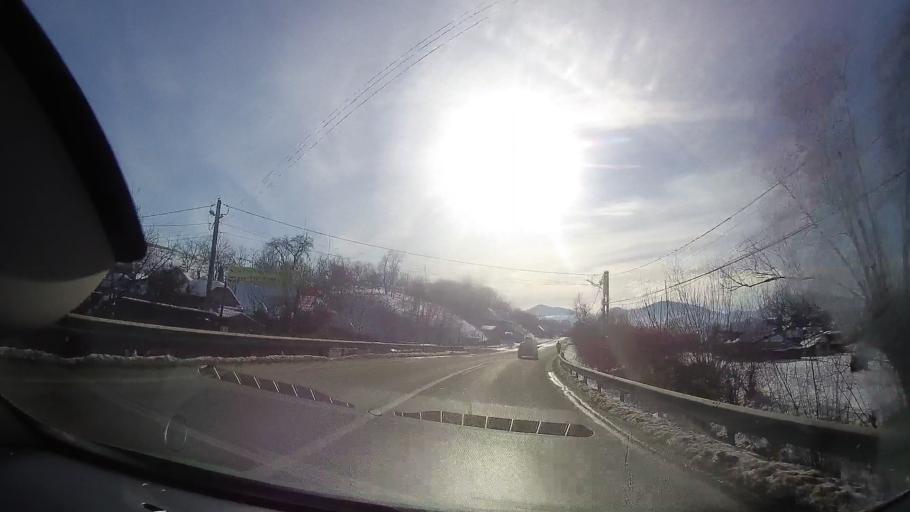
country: RO
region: Neamt
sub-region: Comuna Baltatesti
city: Valea Seaca
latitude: 47.1308
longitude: 26.3154
